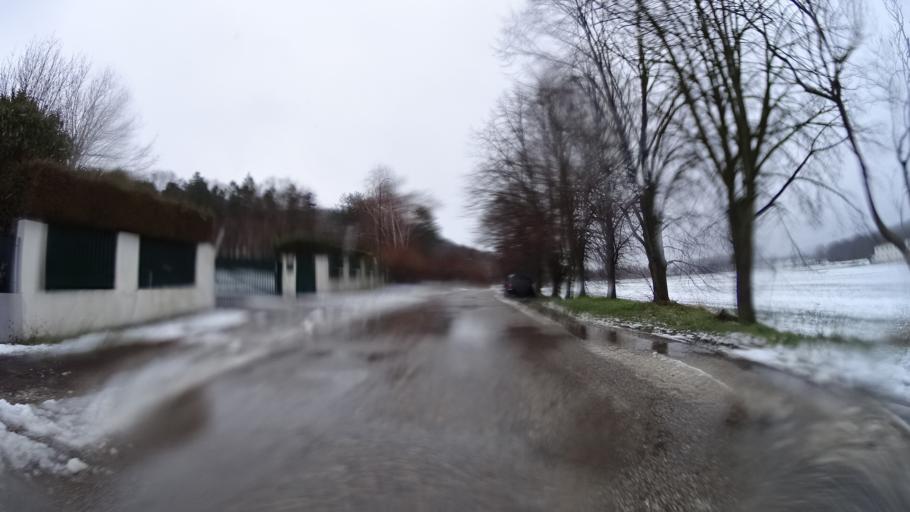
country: AT
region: Lower Austria
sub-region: Politischer Bezirk Korneuburg
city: Leobendorf
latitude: 48.3754
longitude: 16.2956
